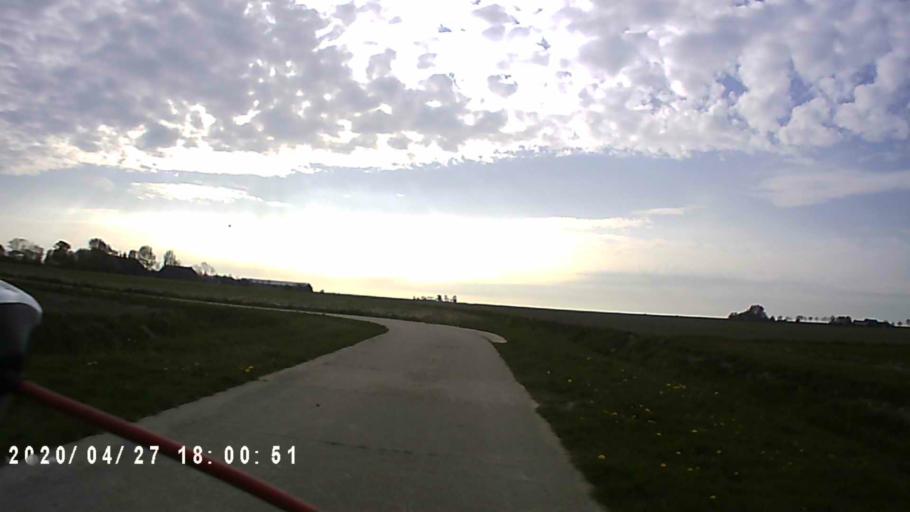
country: NL
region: Groningen
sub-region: Gemeente Winsum
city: Winsum
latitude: 53.4071
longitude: 6.4522
